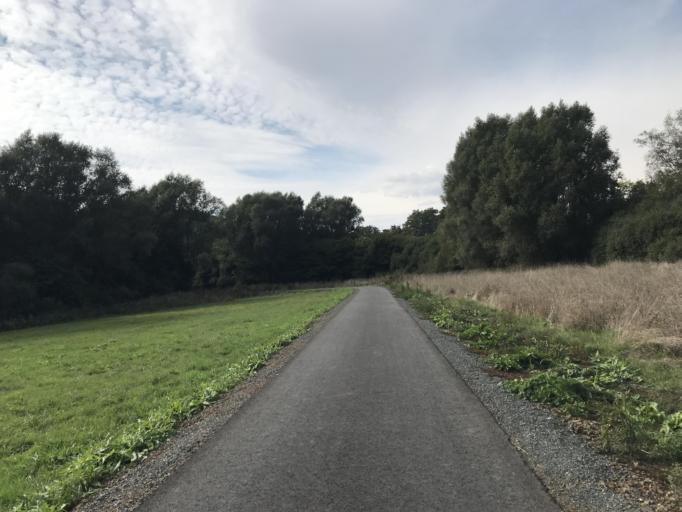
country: DE
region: Hesse
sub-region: Regierungsbezirk Giessen
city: Asslar
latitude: 50.5914
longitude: 8.4524
